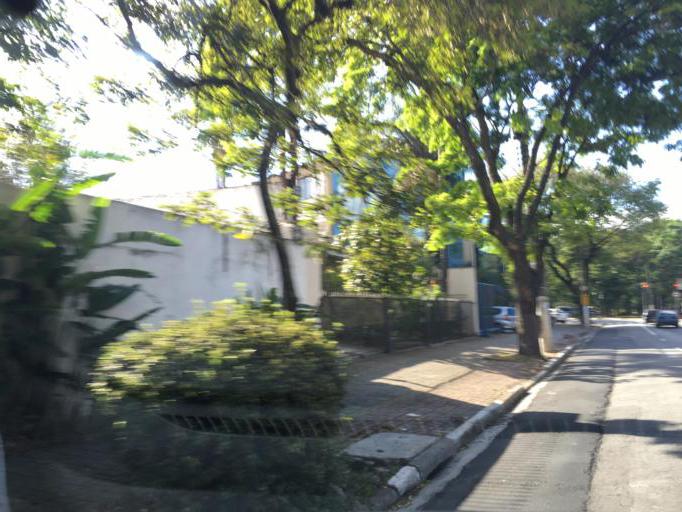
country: BR
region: Sao Paulo
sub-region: Sao Paulo
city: Sao Paulo
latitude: -23.5686
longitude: -46.7083
